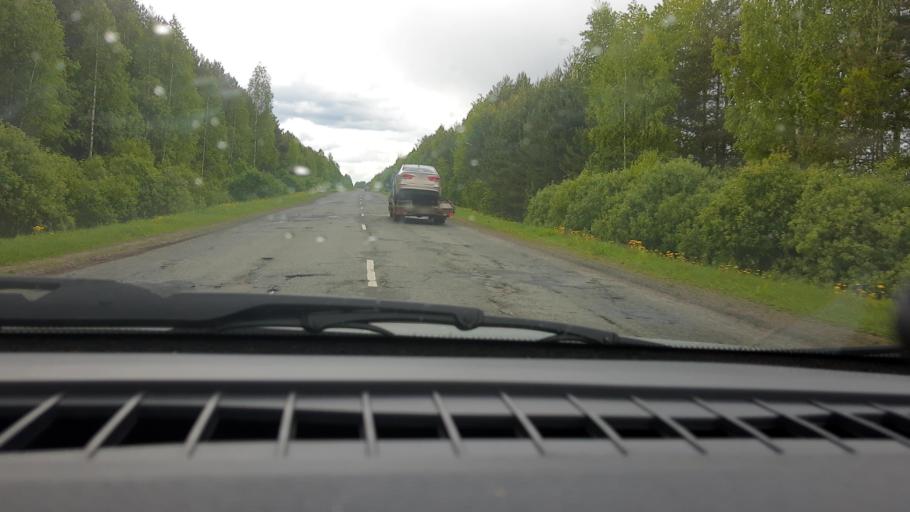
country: RU
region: Nizjnij Novgorod
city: Tonkino
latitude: 57.3588
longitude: 46.3281
